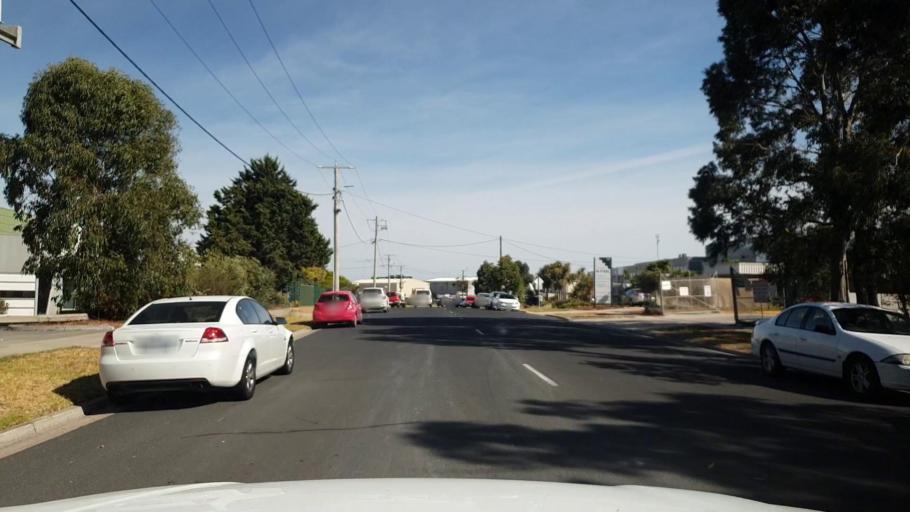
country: AU
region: Victoria
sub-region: Frankston
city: Carrum Downs
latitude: -38.1046
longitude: 145.1628
